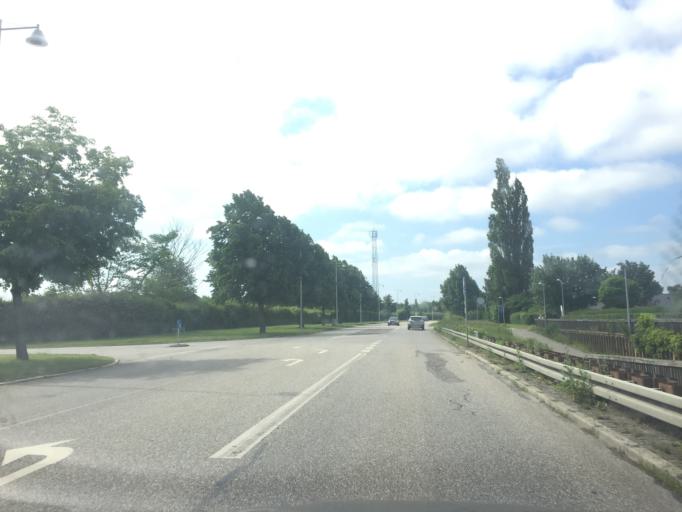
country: DK
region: Capital Region
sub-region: Albertslund Kommune
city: Albertslund
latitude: 55.6660
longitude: 12.3386
